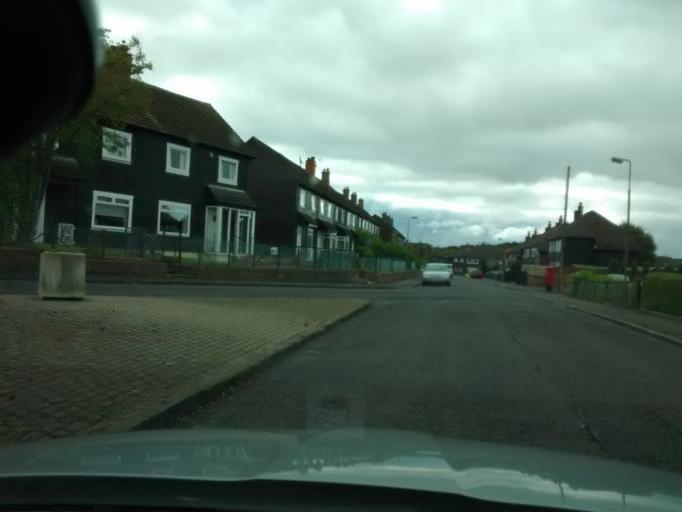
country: GB
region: Scotland
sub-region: West Lothian
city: Bathgate
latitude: 55.9041
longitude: -3.6537
